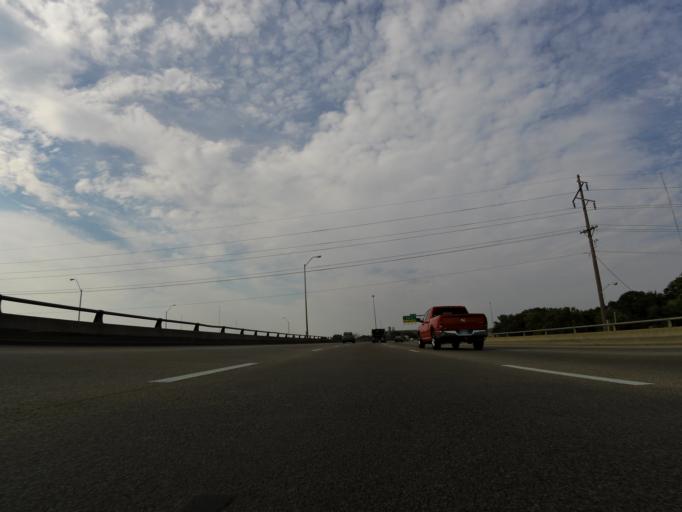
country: US
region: Kansas
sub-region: Sedgwick County
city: Wichita
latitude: 37.7150
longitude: -97.3217
